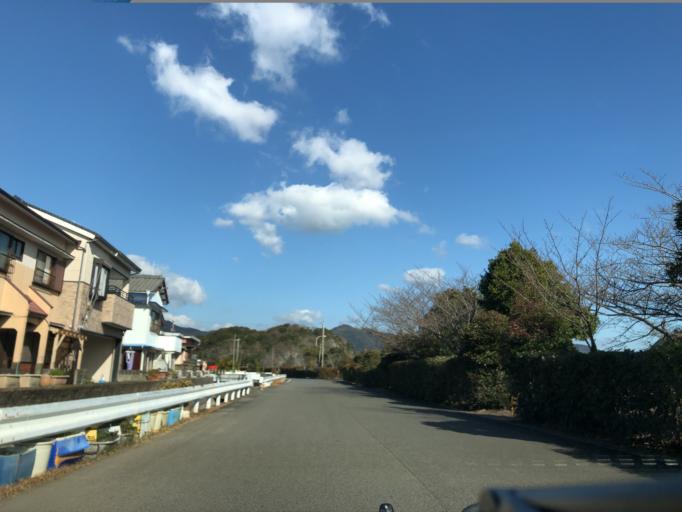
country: JP
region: Kochi
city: Sukumo
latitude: 32.9155
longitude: 132.7044
